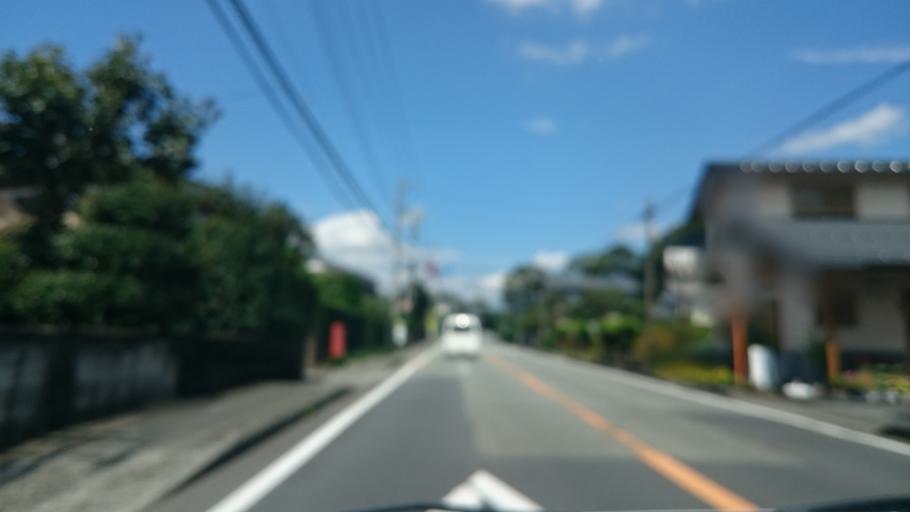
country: JP
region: Shizuoka
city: Gotemba
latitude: 35.2621
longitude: 138.9232
